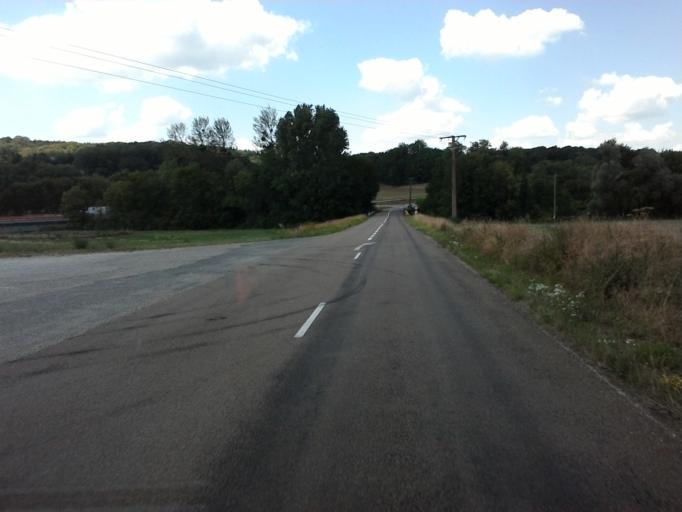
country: FR
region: Franche-Comte
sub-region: Departement du Jura
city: Montmorot
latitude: 46.7678
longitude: 5.5577
